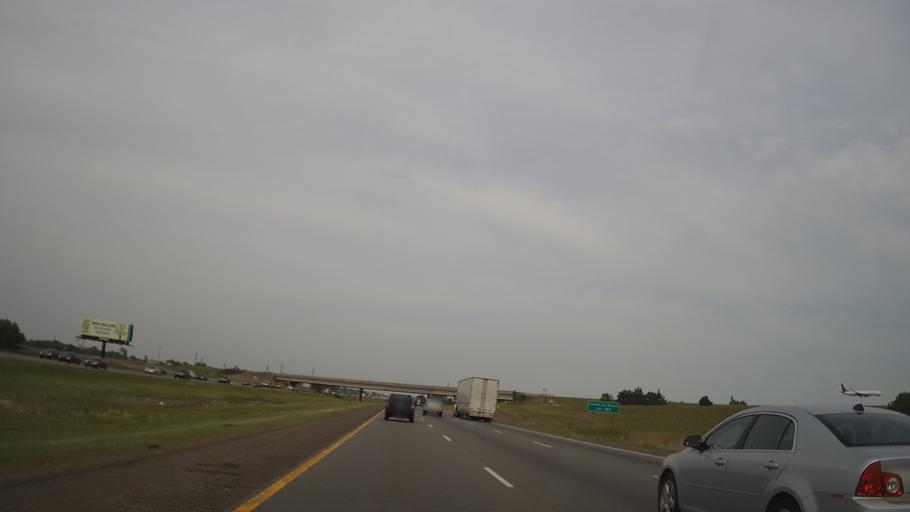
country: US
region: Michigan
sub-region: Wayne County
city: Romulus
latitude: 42.2312
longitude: -83.3728
